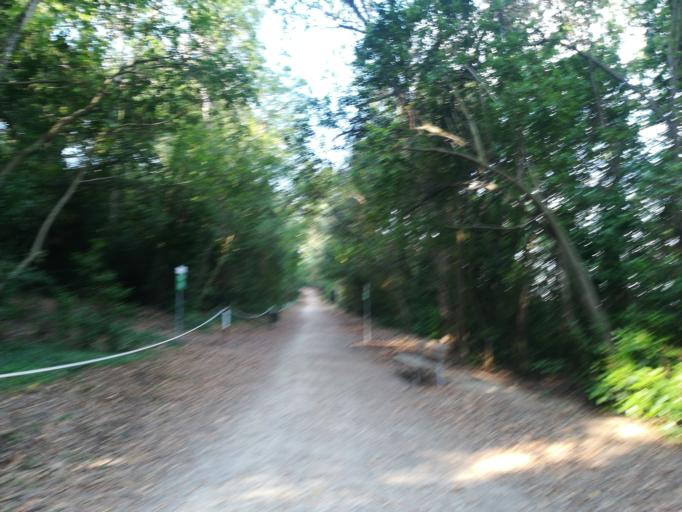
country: IT
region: The Marches
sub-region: Provincia di Macerata
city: Villa Potenza
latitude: 43.2960
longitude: 13.4227
